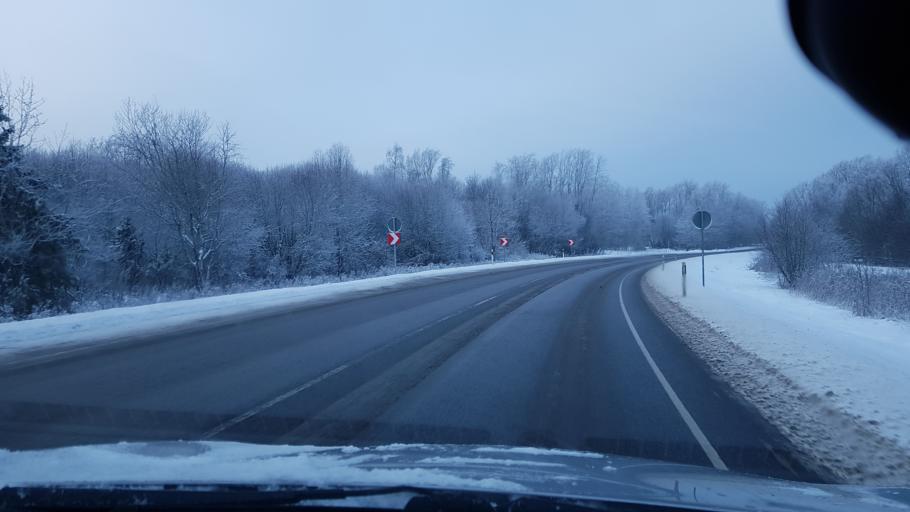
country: EE
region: Harju
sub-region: Paldiski linn
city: Paldiski
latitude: 59.3397
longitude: 24.2035
